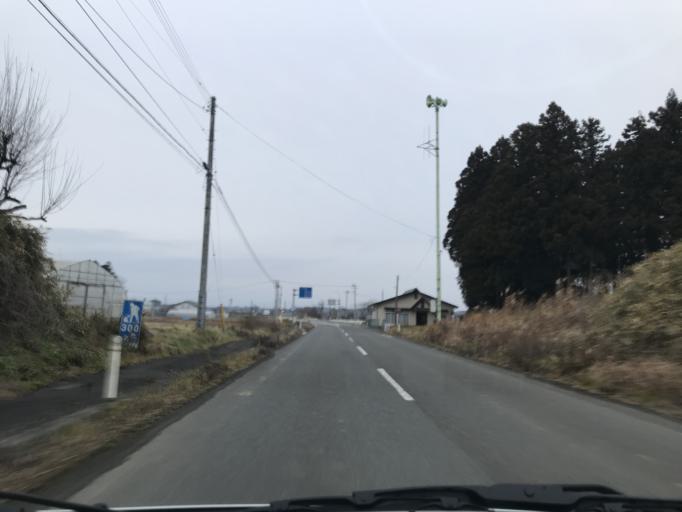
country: JP
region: Miyagi
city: Kogota
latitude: 38.7032
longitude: 141.0980
